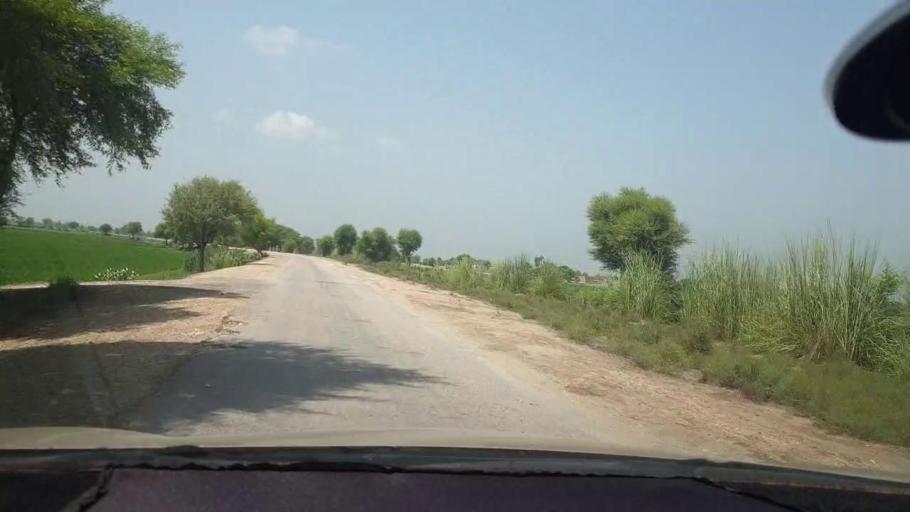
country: PK
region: Sindh
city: Kambar
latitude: 27.6634
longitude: 67.9189
